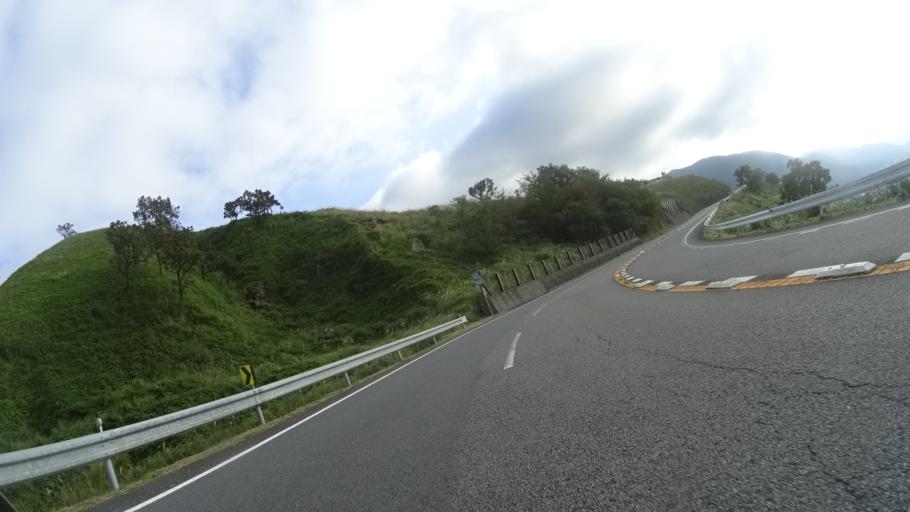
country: JP
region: Oita
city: Beppu
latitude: 33.2632
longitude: 131.3848
